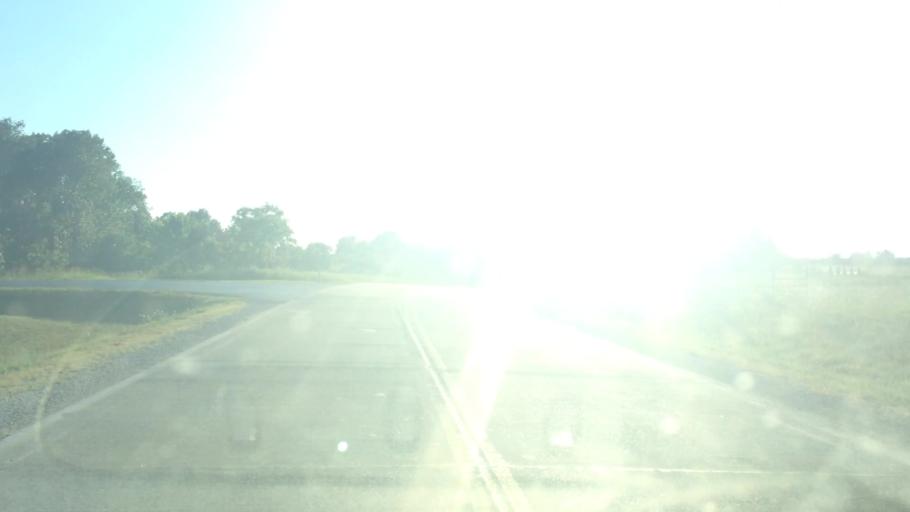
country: US
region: Missouri
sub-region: Greene County
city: Strafford
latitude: 37.2489
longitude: -93.1838
